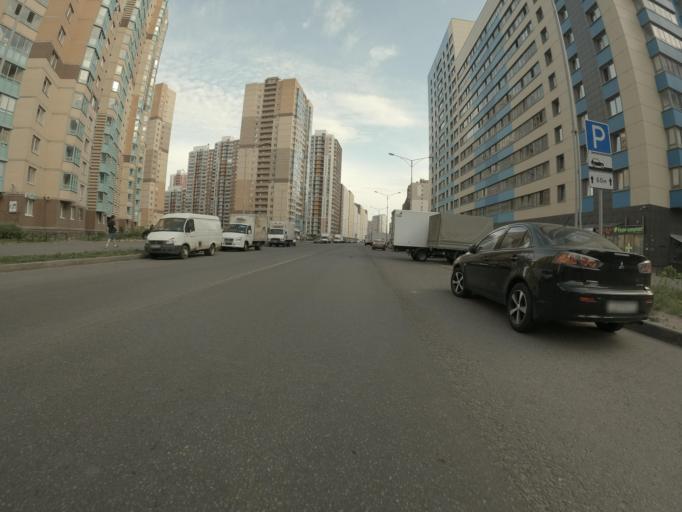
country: RU
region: Leningrad
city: Rybatskoye
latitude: 59.9043
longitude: 30.5127
